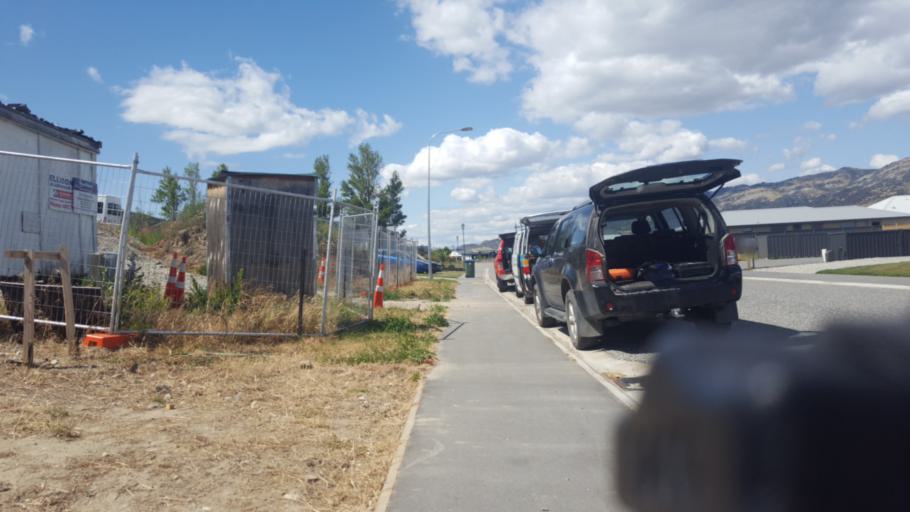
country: NZ
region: Otago
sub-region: Queenstown-Lakes District
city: Wanaka
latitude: -44.9739
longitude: 169.2419
